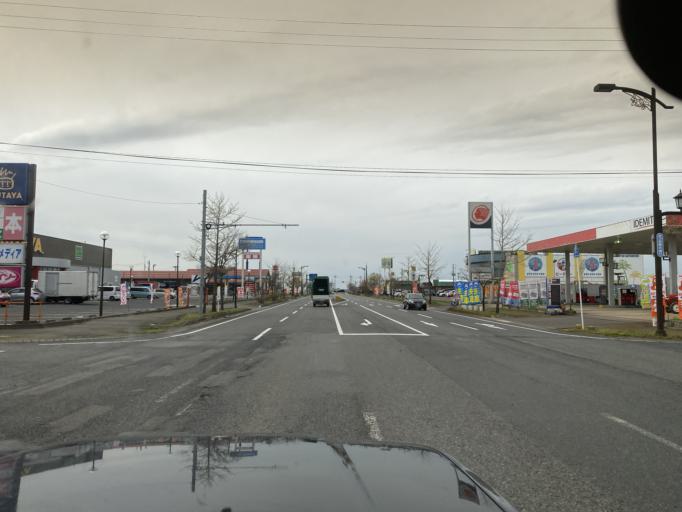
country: JP
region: Niigata
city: Niitsu-honcho
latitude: 37.8154
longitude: 139.1033
